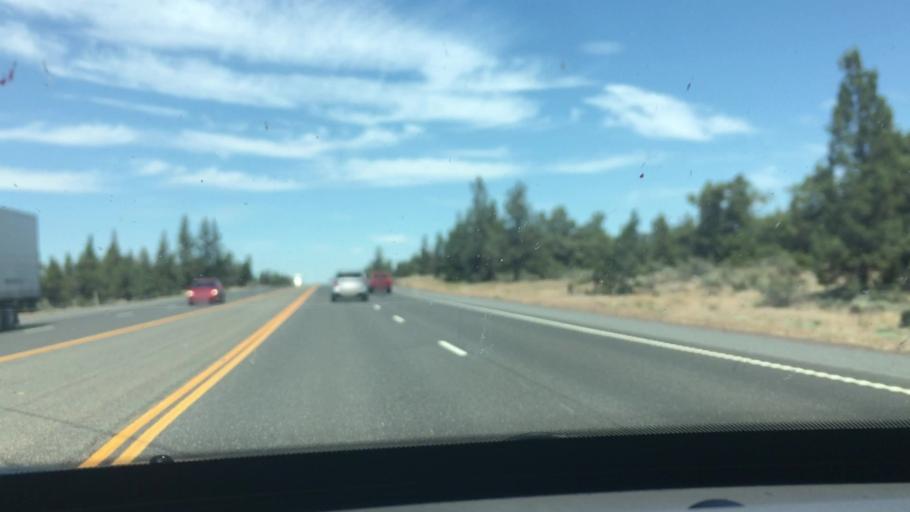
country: US
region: Oregon
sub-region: Deschutes County
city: Redmond
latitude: 44.1818
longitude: -121.2435
